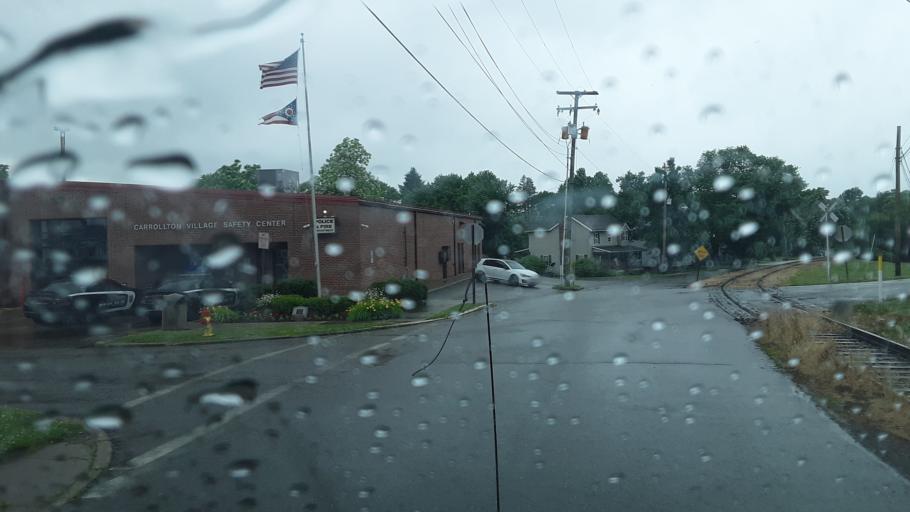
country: US
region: Ohio
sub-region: Carroll County
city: Carrollton
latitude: 40.5721
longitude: -81.0889
